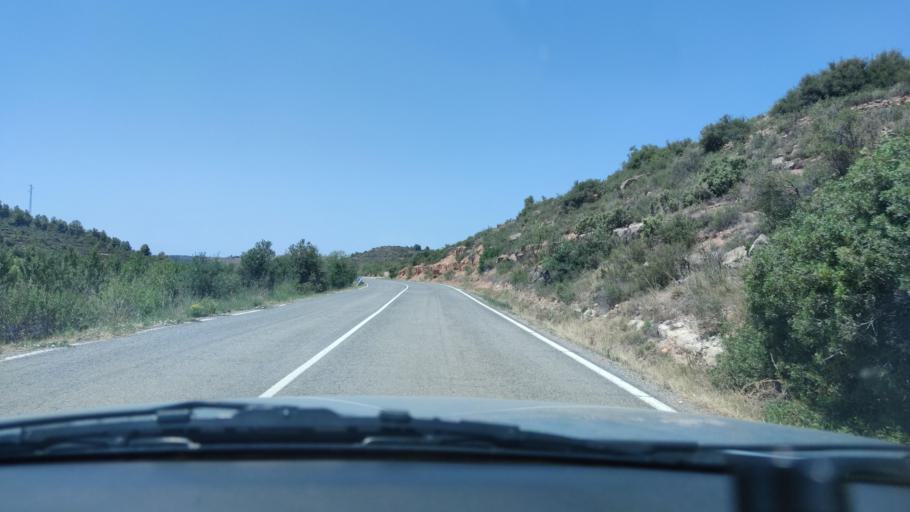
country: ES
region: Catalonia
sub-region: Provincia de Lleida
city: el Cogul
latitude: 41.4240
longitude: 0.6726
